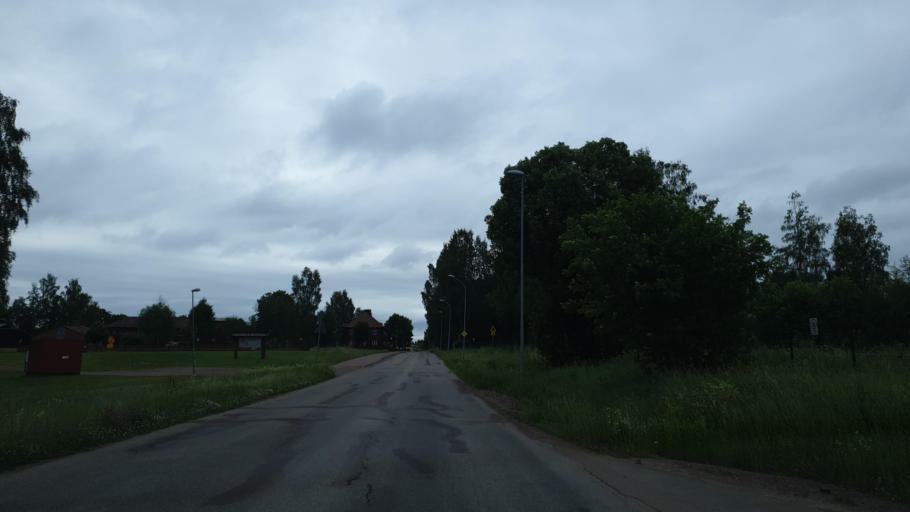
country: SE
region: Dalarna
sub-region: Mora Kommun
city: Mora
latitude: 60.9992
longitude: 14.5416
